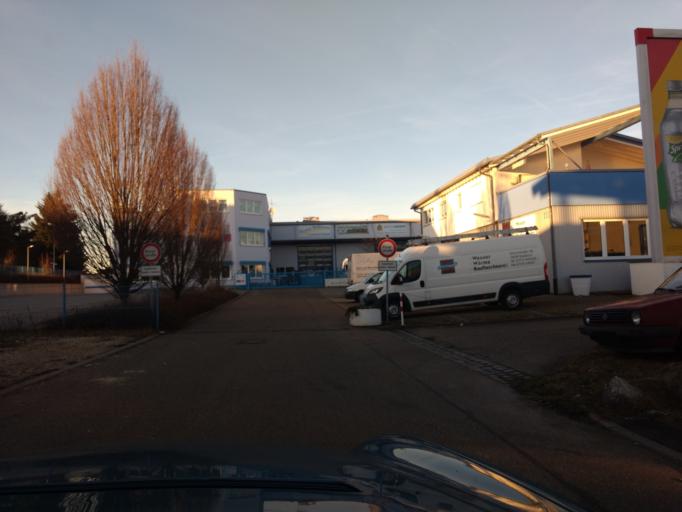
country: DE
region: Baden-Wuerttemberg
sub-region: Regierungsbezirk Stuttgart
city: Schwabisch Gmund
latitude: 48.7858
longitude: 9.7987
